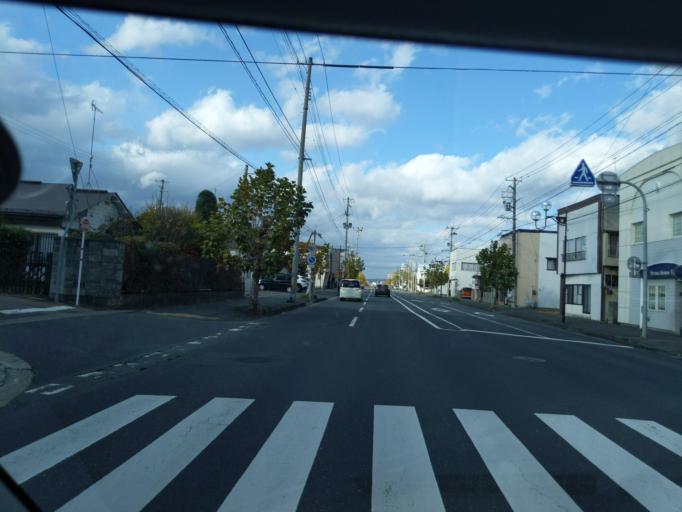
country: JP
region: Iwate
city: Mizusawa
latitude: 39.1372
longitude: 141.1552
